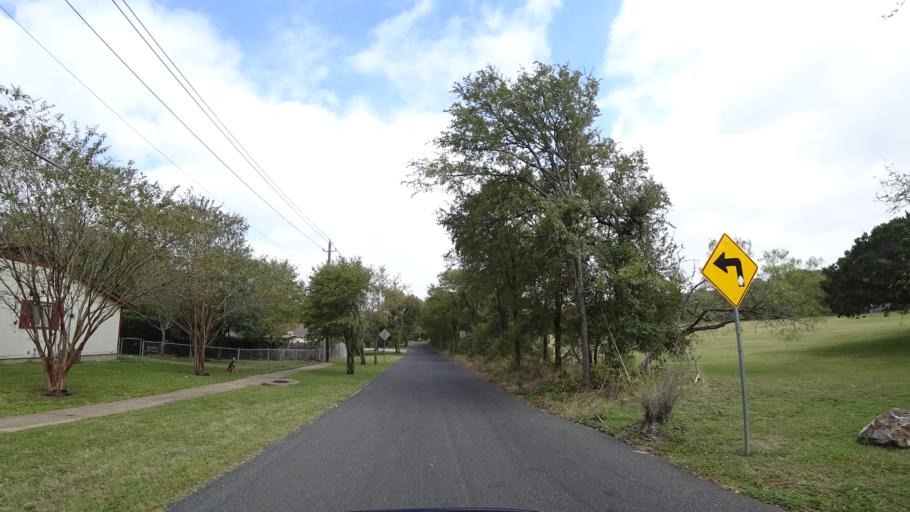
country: US
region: Texas
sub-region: Travis County
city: Shady Hollow
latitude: 30.2034
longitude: -97.8271
